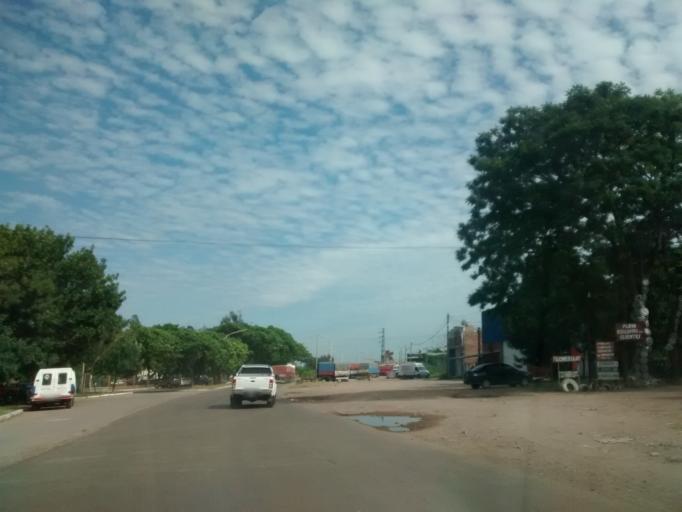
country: AR
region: Chaco
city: Fontana
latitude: -27.4330
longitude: -59.0089
